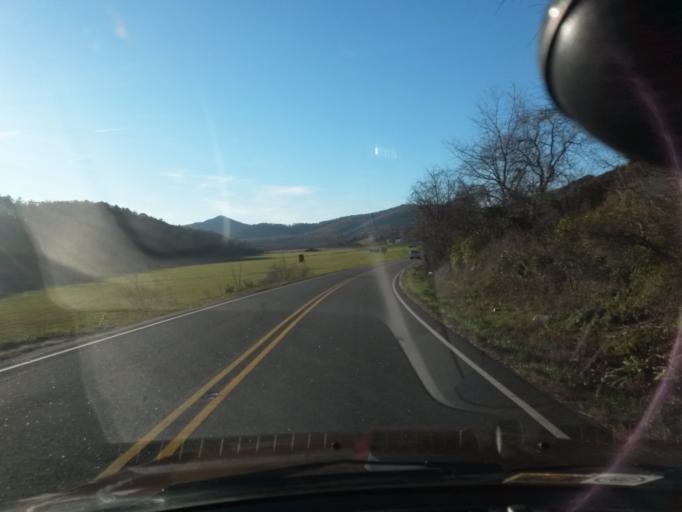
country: US
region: Virginia
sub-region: Amherst County
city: Amherst
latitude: 37.6650
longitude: -79.1834
